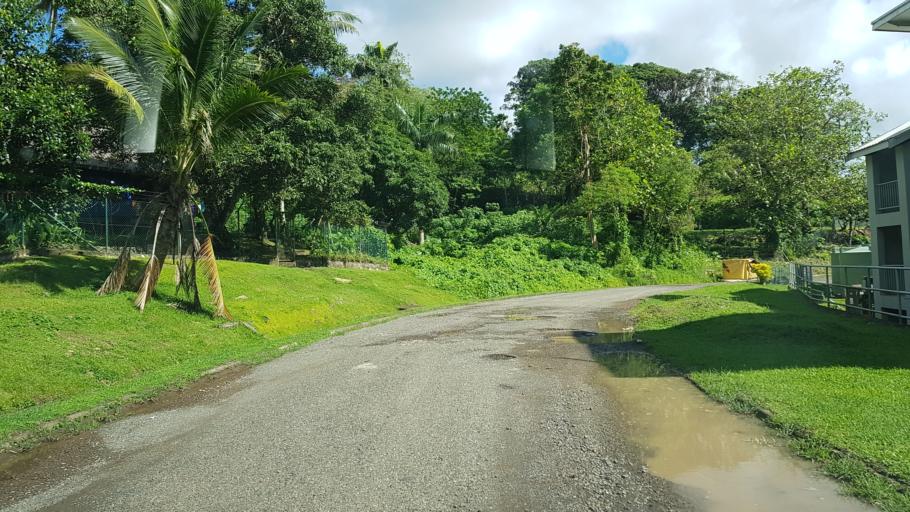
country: FJ
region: Central
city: Suva
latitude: -18.1494
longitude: 178.4406
